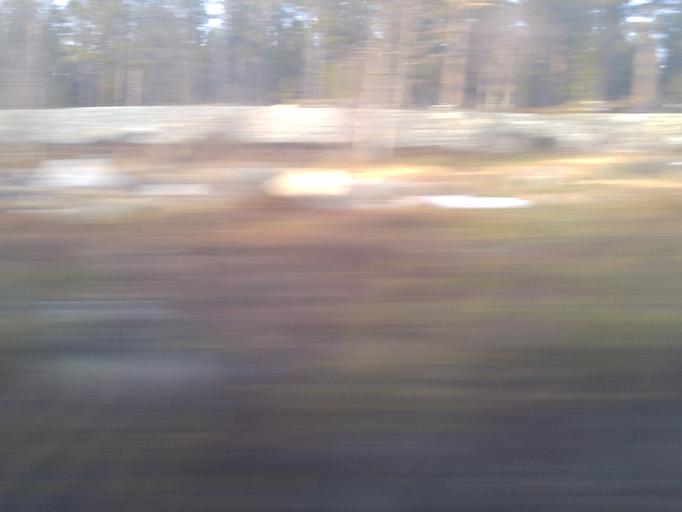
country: NO
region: Oppland
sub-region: Dovre
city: Dombas
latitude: 62.1023
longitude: 9.1384
